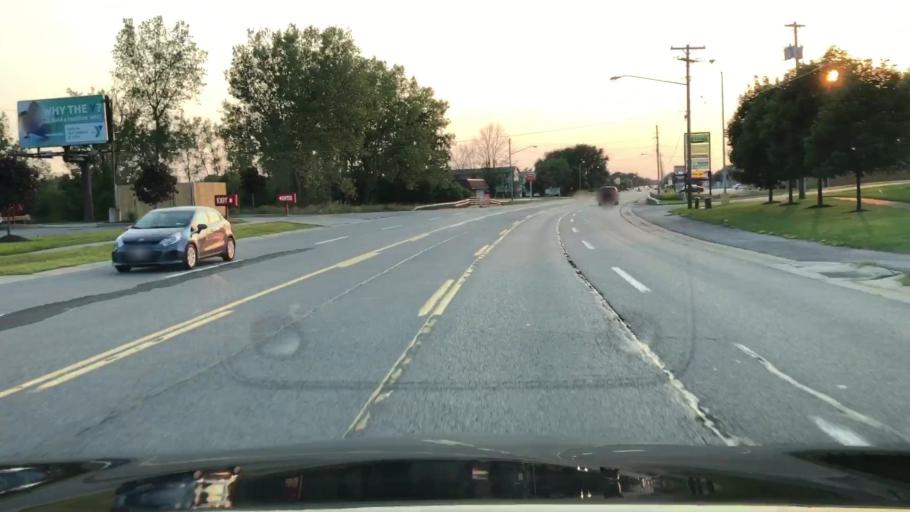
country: US
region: New York
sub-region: Erie County
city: Depew
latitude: 42.8680
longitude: -78.6997
